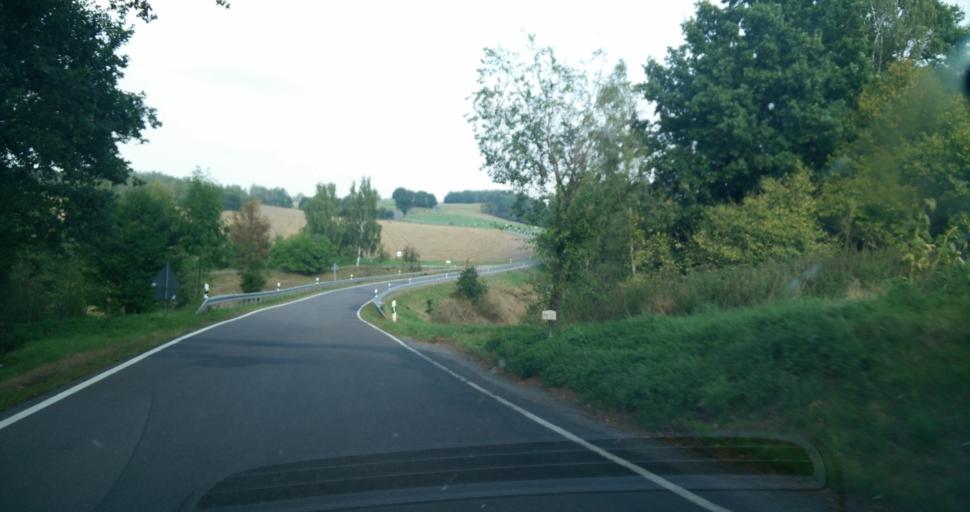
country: DE
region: Saxony
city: Rochlitz
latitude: 51.0768
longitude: 12.7885
